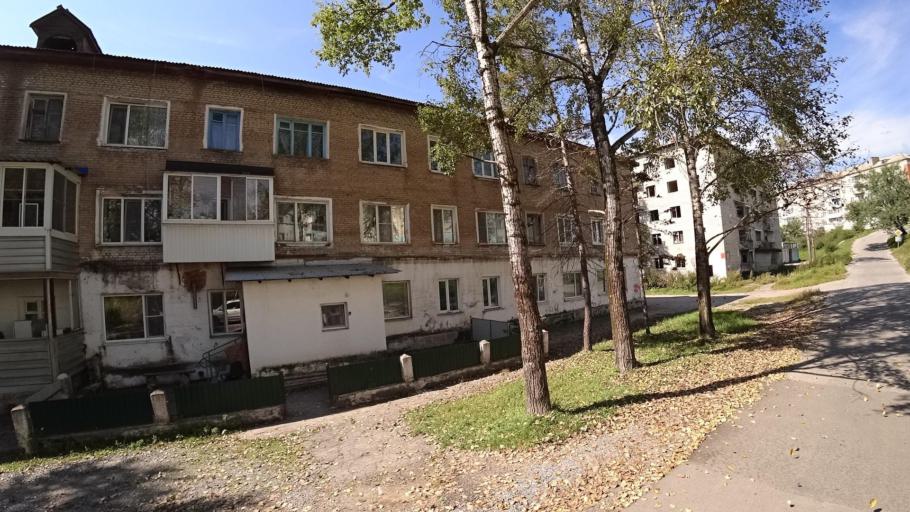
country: RU
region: Jewish Autonomous Oblast
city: Londoko
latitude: 49.0121
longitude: 131.8829
